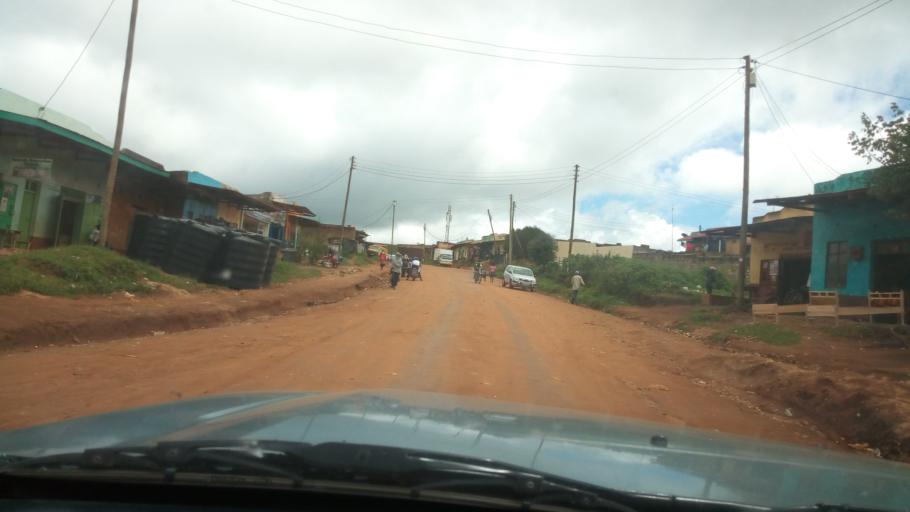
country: KE
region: Makueni
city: Wote
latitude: -1.6642
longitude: 37.4479
